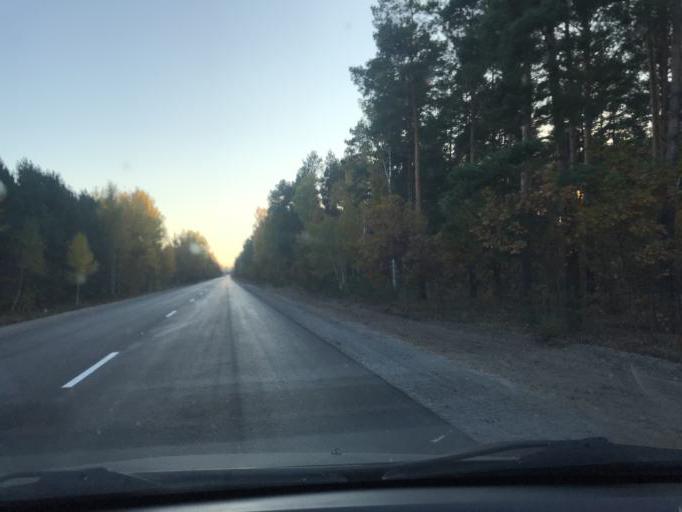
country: BY
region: Gomel
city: Brahin
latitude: 51.8702
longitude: 30.3792
